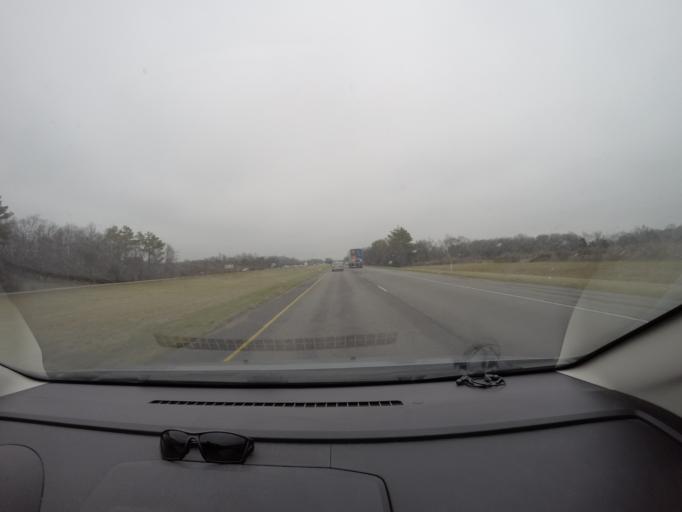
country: US
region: Tennessee
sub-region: Rutherford County
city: Plainview
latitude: 35.7689
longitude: -86.3606
